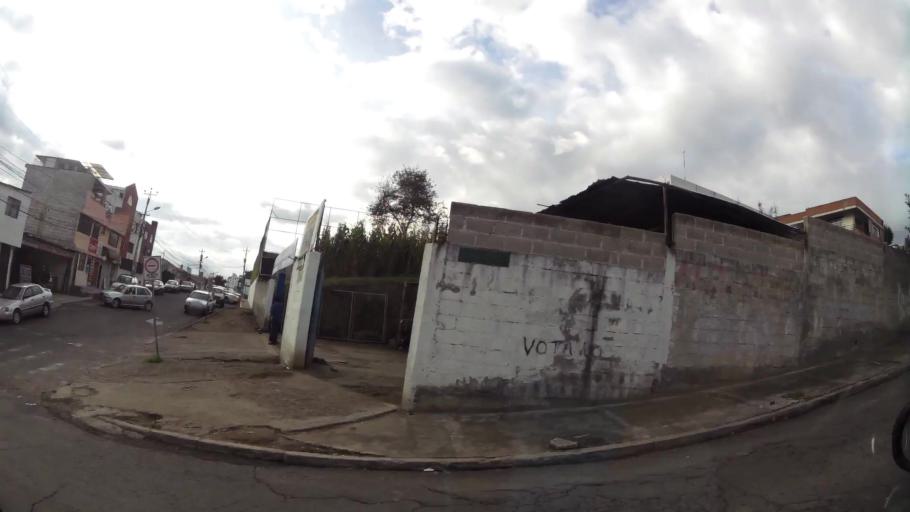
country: EC
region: Pichincha
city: Quito
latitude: -0.1440
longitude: -78.4673
